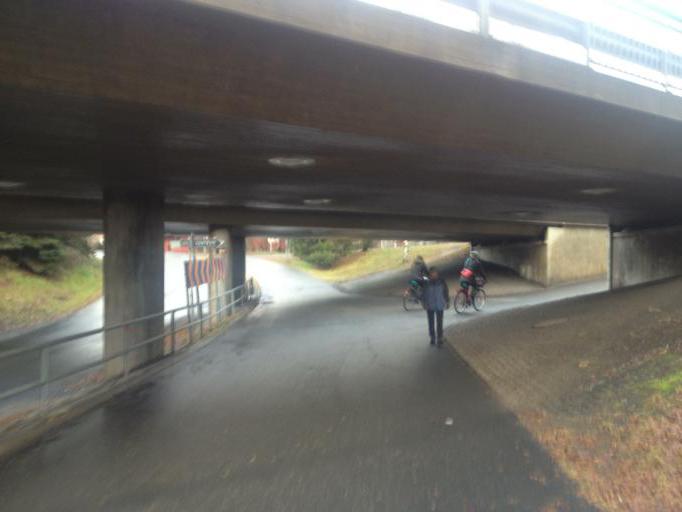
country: SE
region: Vaesterbotten
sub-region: Umea Kommun
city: Umea
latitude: 63.8189
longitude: 20.2644
